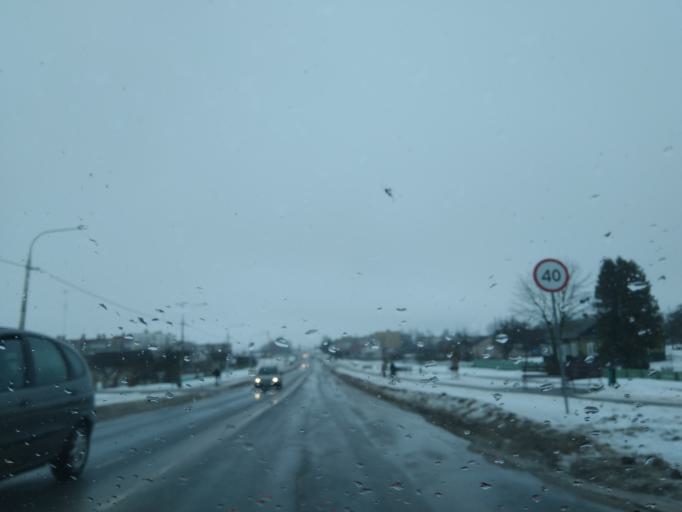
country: BY
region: Minsk
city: Nyasvizh
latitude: 53.2332
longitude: 26.6513
